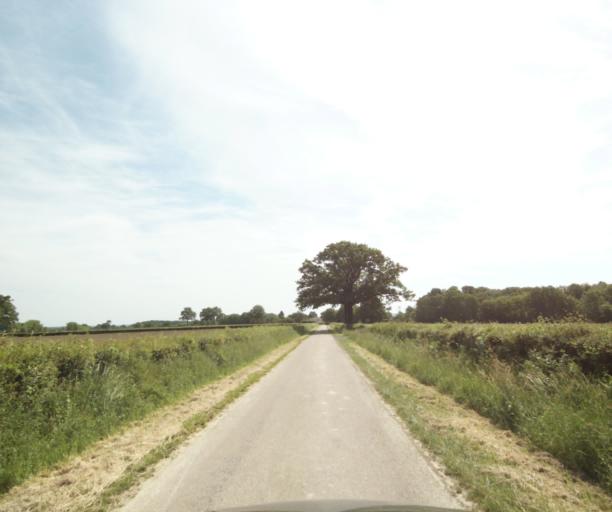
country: FR
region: Bourgogne
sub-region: Departement de Saone-et-Loire
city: Palinges
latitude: 46.5429
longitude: 4.1678
